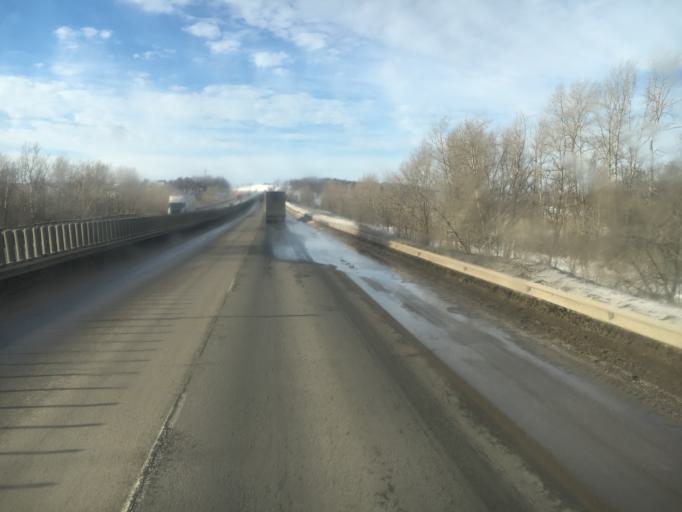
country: RU
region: Samara
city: Mirnyy
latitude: 53.4422
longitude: 50.2727
